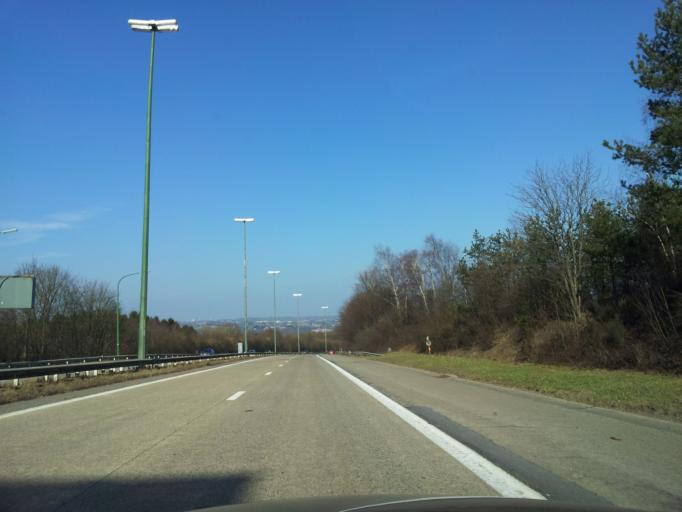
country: BE
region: Wallonia
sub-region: Province de Liege
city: Verviers
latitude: 50.5633
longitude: 5.8572
